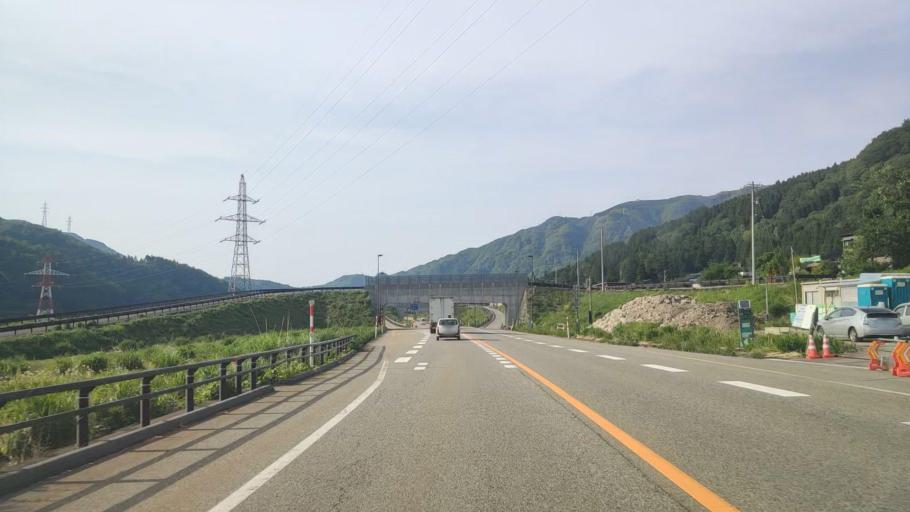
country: JP
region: Toyama
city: Yatsuomachi-higashikumisaka
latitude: 36.5184
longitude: 137.2310
